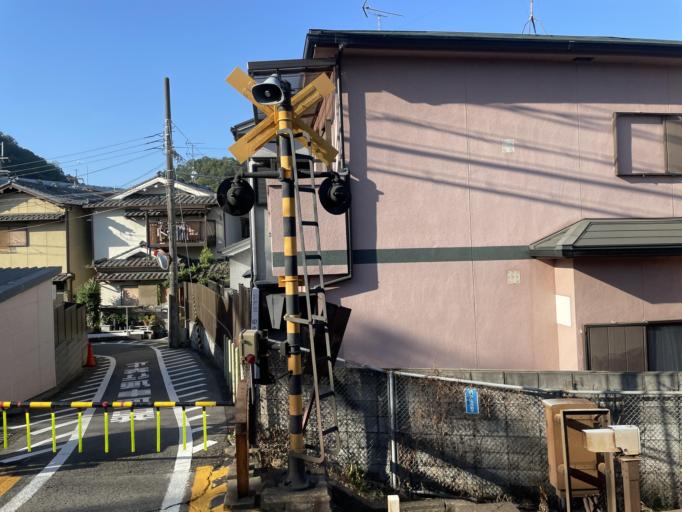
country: JP
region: Osaka
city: Kashihara
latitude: 34.5570
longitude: 135.6423
